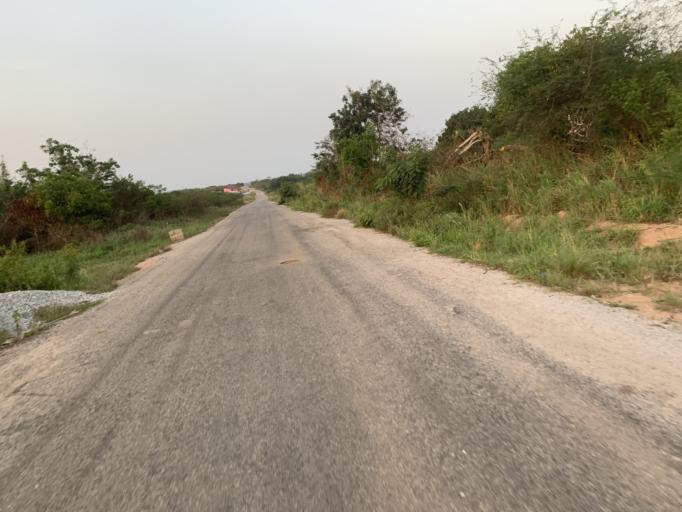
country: GH
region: Central
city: Winneba
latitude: 5.3730
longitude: -0.6145
